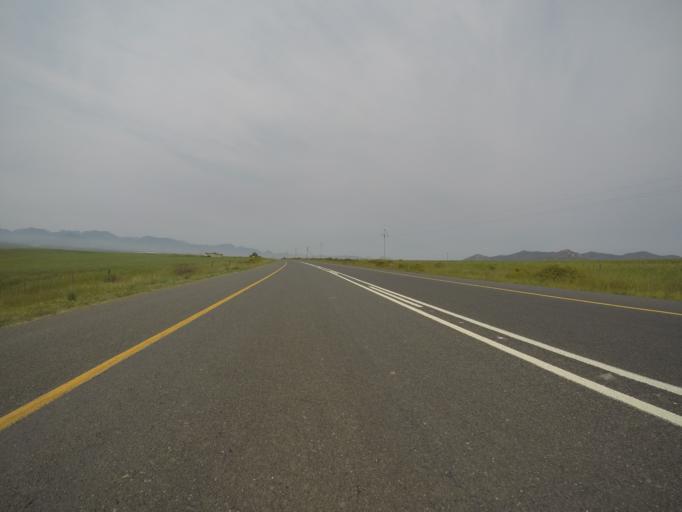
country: ZA
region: Western Cape
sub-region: West Coast District Municipality
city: Malmesbury
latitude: -33.5277
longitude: 18.8483
